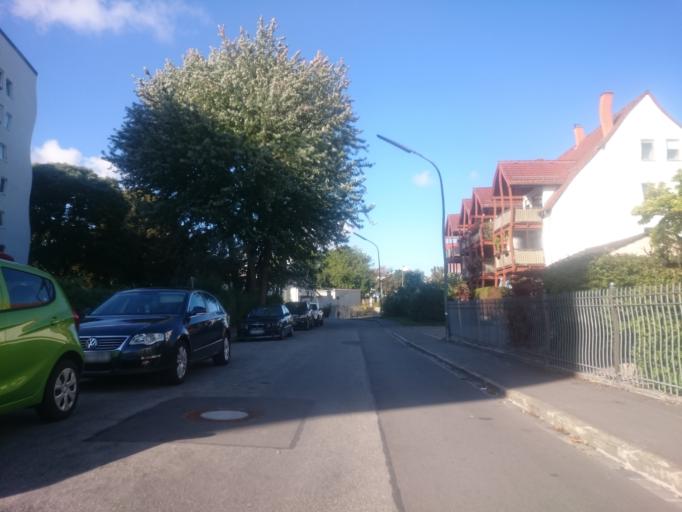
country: DE
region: Bavaria
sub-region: Swabia
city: Augsburg
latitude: 48.3740
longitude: 10.9290
